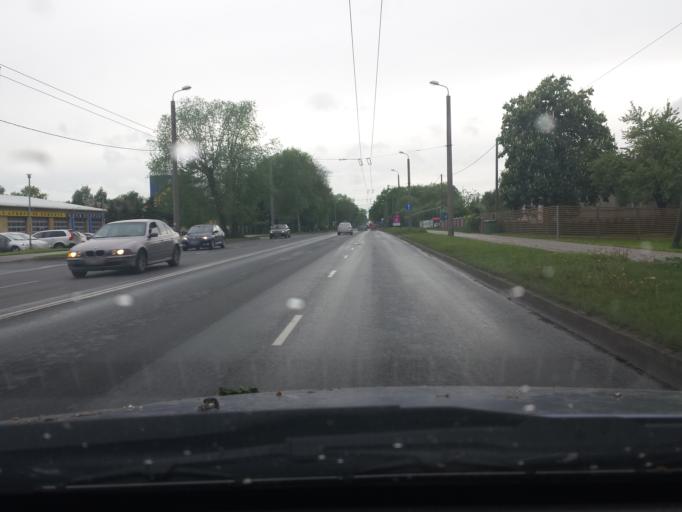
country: LV
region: Riga
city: Riga
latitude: 56.9497
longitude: 24.1819
